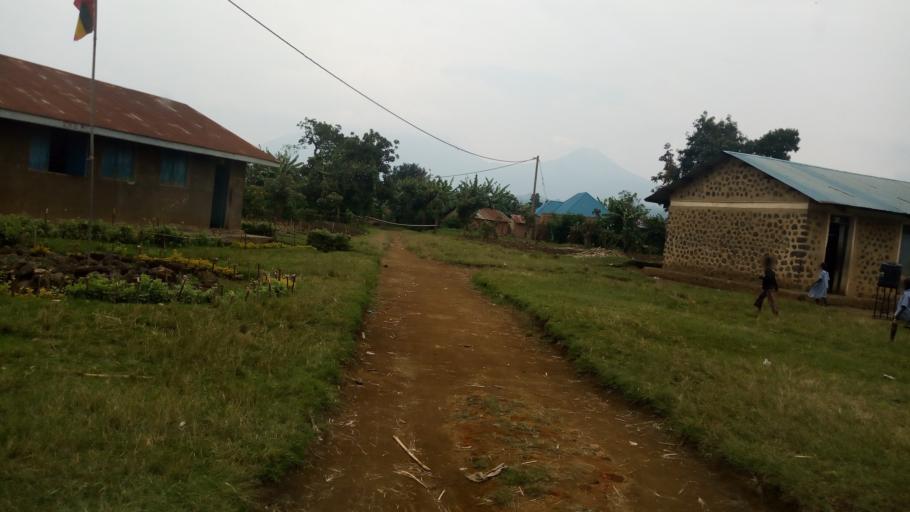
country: UG
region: Western Region
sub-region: Kisoro District
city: Kisoro
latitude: -1.2750
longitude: 29.6230
